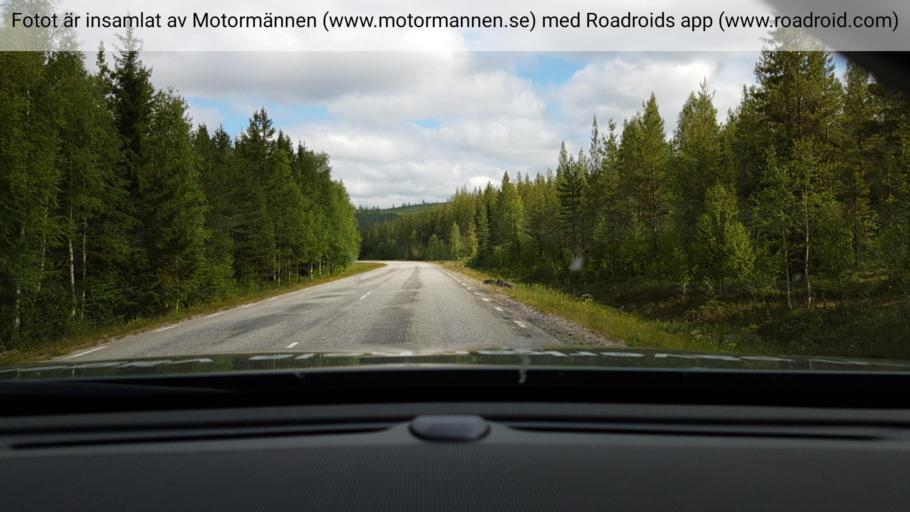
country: SE
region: Vaesterbotten
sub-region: Mala Kommun
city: Mala
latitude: 64.9354
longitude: 18.6227
